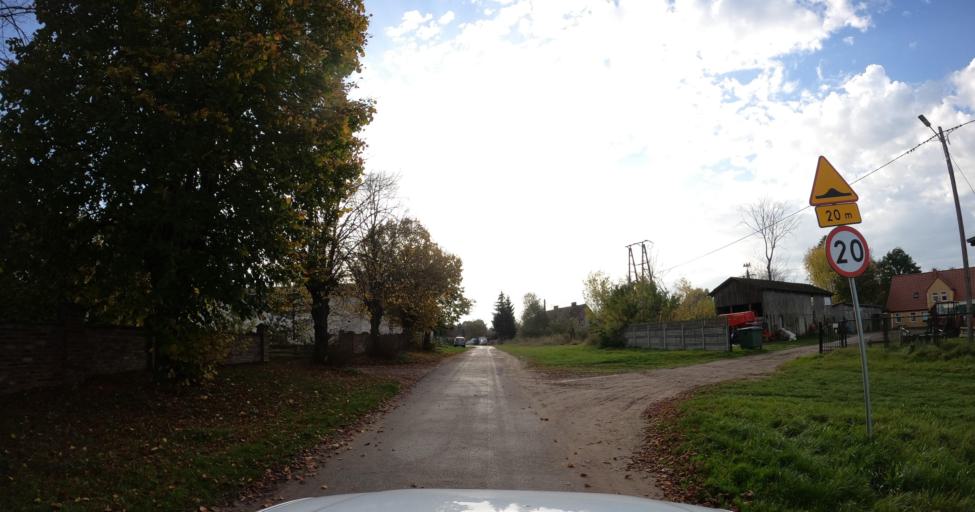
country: PL
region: West Pomeranian Voivodeship
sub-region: Powiat kamienski
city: Golczewo
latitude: 53.8599
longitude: 14.9115
